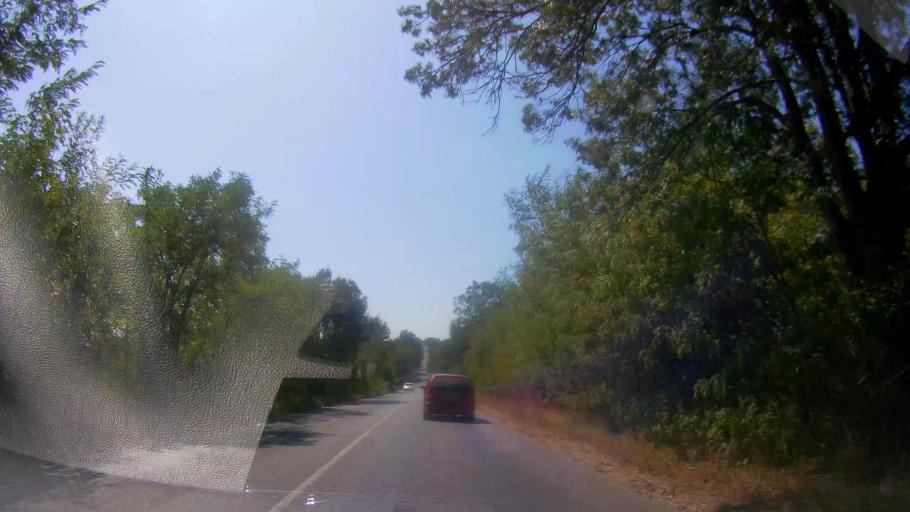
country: BG
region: Veliko Turnovo
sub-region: Obshtina Gorna Oryakhovitsa
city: Purvomaytsi
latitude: 43.2436
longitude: 25.6433
